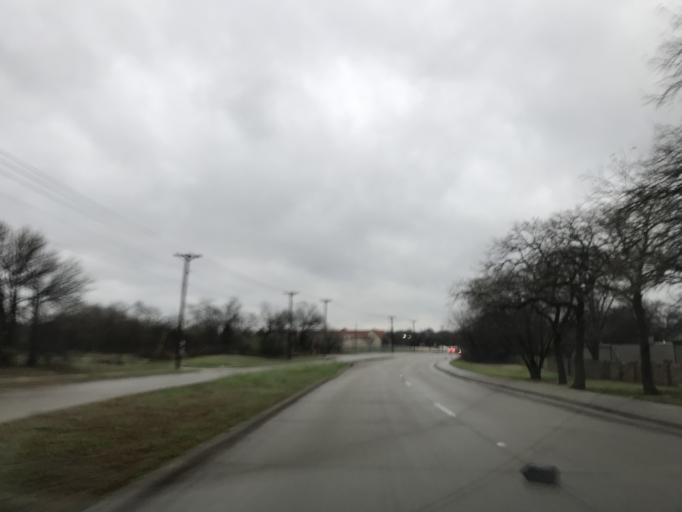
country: US
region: Texas
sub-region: Dallas County
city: Grand Prairie
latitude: 32.7715
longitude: -97.0473
